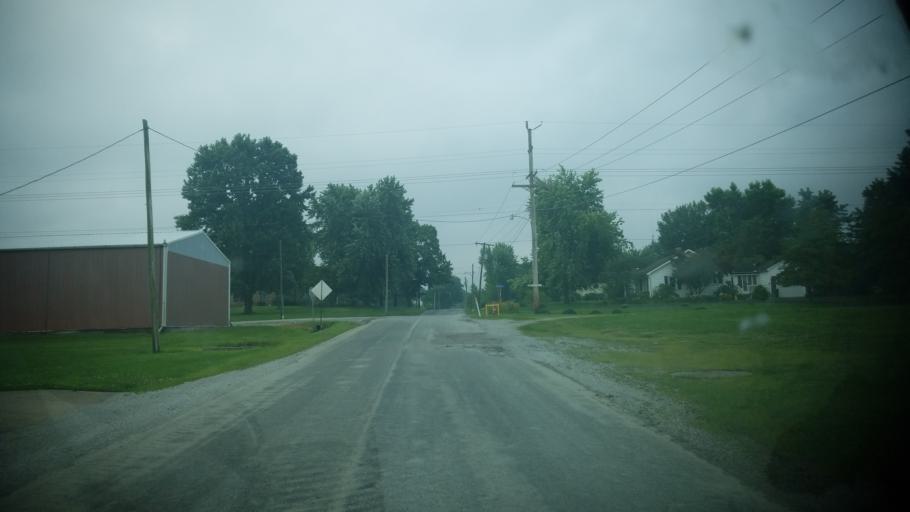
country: US
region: Illinois
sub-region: Clay County
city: Flora
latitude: 38.6784
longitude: -88.3541
